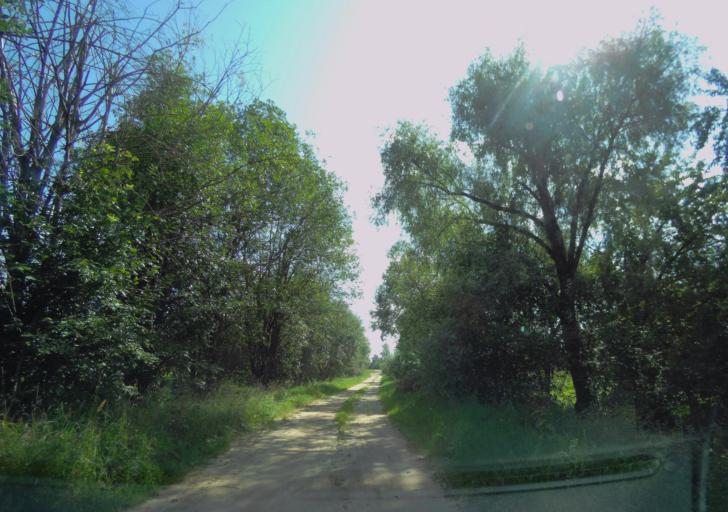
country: BY
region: Minsk
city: Zyembin
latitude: 54.4124
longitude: 28.3796
